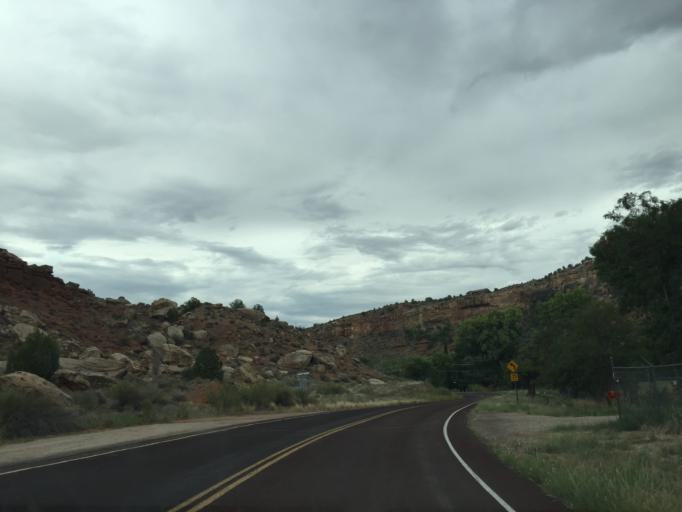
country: US
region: Utah
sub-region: Washington County
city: Hildale
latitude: 37.1610
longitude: -113.0317
